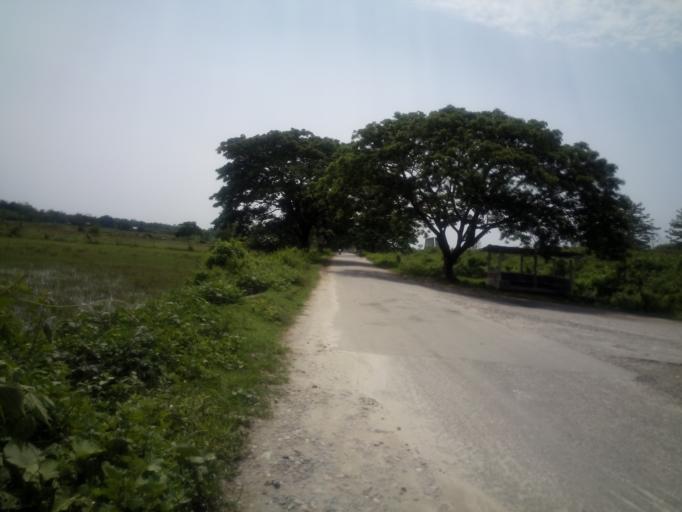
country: IN
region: Assam
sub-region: Udalguri
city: Udalguri
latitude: 26.7432
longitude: 92.1312
